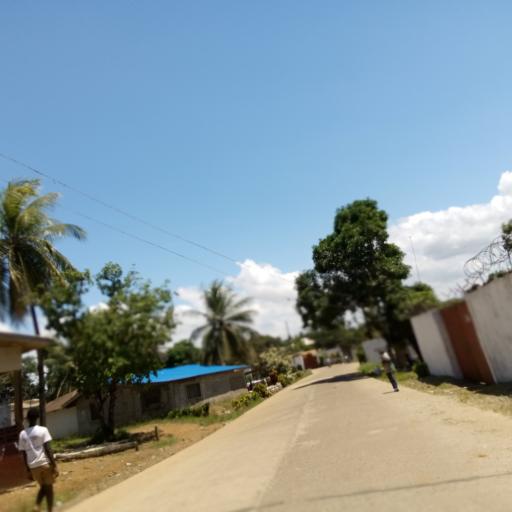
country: LR
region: Montserrado
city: Monrovia
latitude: 6.2452
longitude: -10.6919
